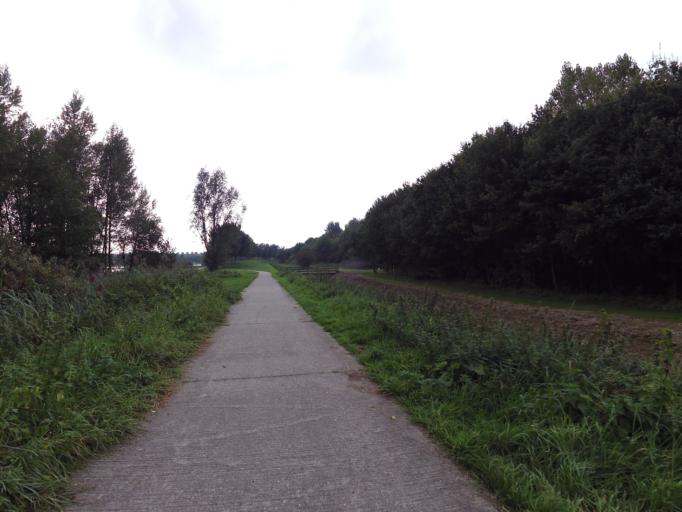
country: NL
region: Gelderland
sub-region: Gemeente Westervoort
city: Westervoort
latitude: 51.9521
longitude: 5.9921
